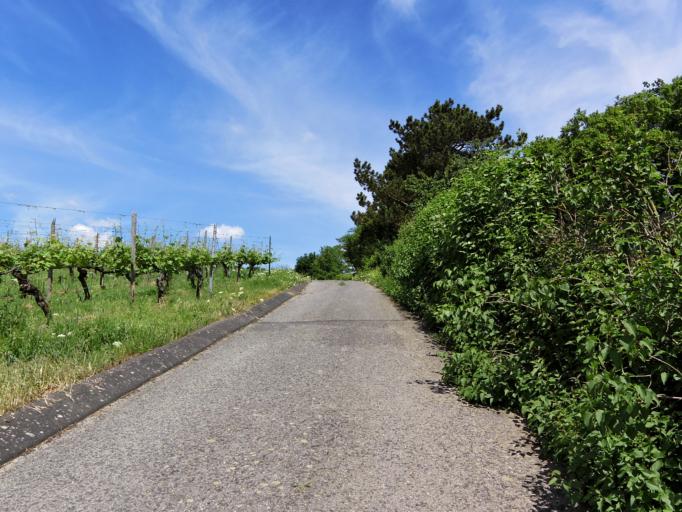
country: DE
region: Bavaria
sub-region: Regierungsbezirk Unterfranken
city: Wuerzburg
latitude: 49.8080
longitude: 9.9398
